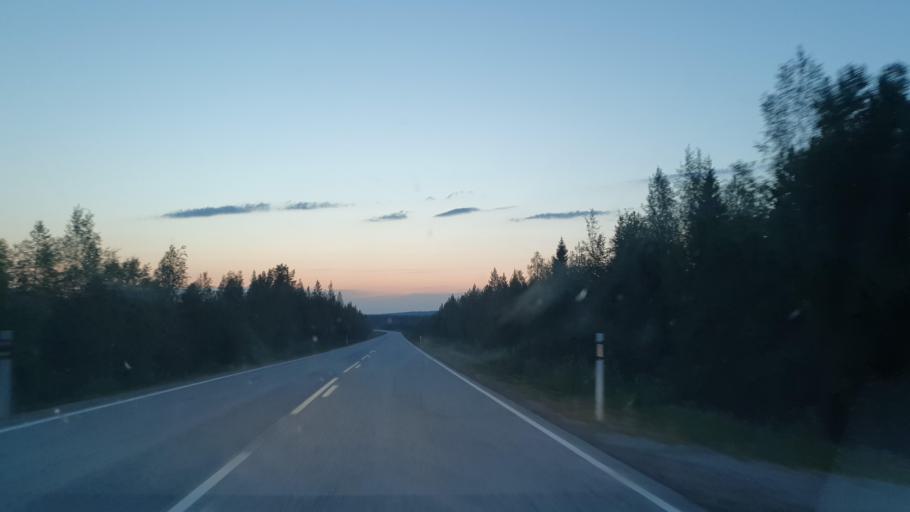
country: FI
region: Northern Ostrobothnia
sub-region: Koillismaa
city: Kuusamo
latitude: 65.4880
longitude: 28.9465
